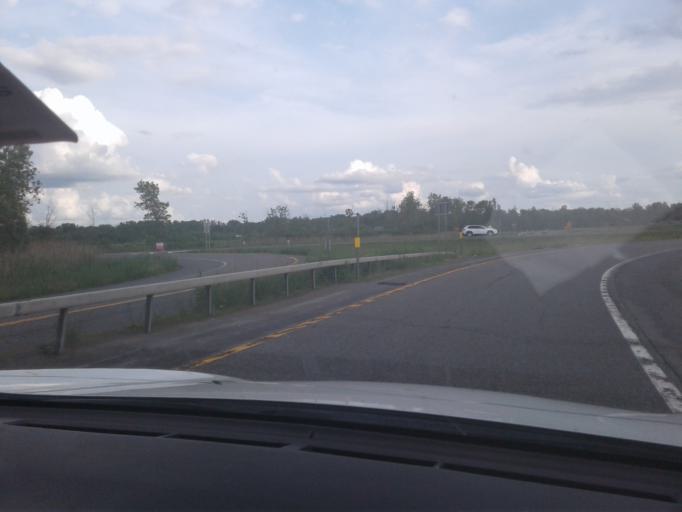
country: US
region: New York
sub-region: Onondaga County
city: East Syracuse
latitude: 43.0787
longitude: -76.0514
